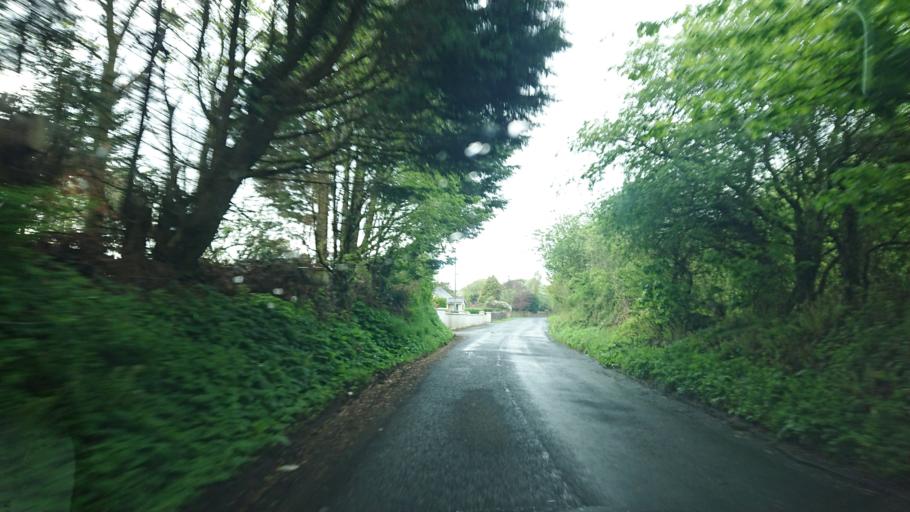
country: IE
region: Munster
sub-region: Waterford
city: Waterford
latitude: 52.2338
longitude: -7.0776
